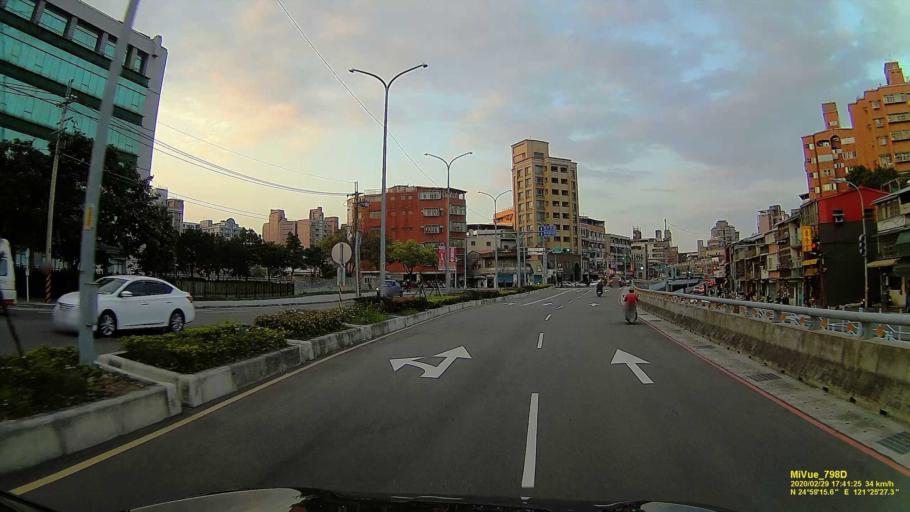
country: TW
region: Taipei
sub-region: Taipei
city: Banqiao
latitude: 24.9879
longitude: 121.4243
